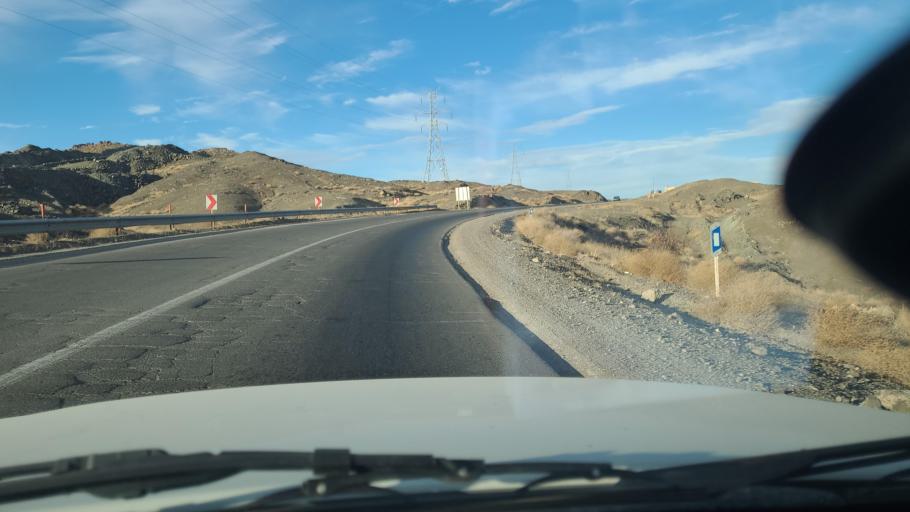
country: IR
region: Razavi Khorasan
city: Sabzevar
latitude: 36.4037
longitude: 57.5477
